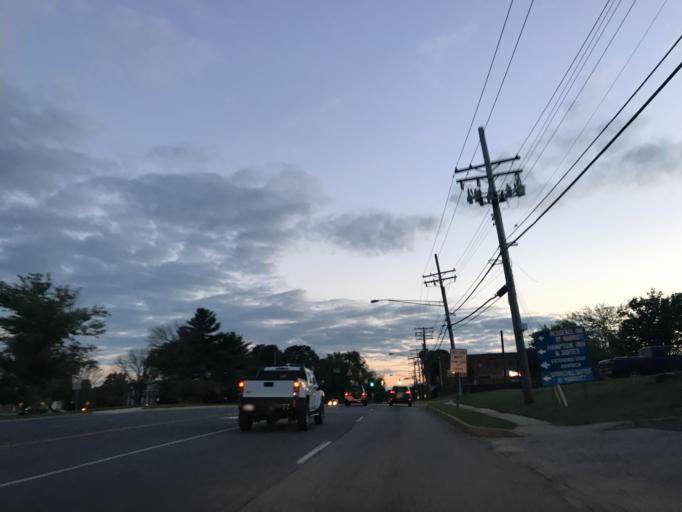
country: US
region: Maryland
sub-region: Anne Arundel County
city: Parole
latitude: 38.9784
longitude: -76.5505
